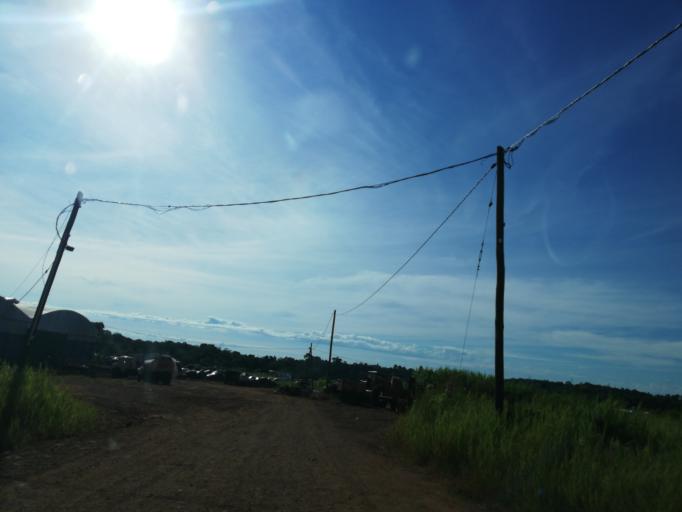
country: AR
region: Misiones
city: Dos de Mayo
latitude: -26.9912
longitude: -54.4966
